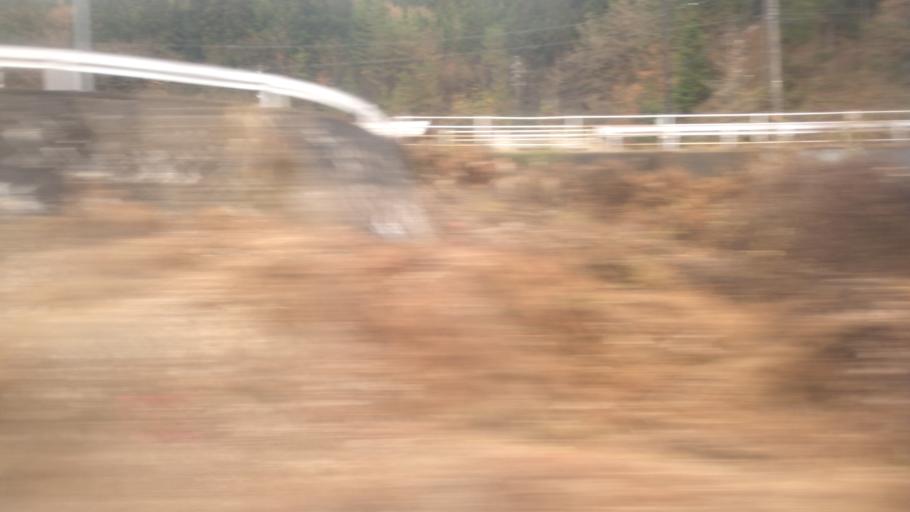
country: JP
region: Nagano
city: Iida
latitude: 35.6818
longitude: 137.6519
